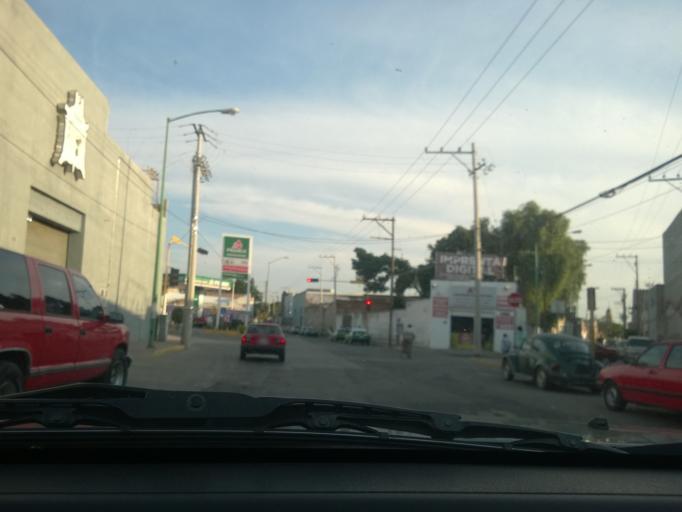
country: MX
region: Guanajuato
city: Leon
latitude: 21.1357
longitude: -101.6812
